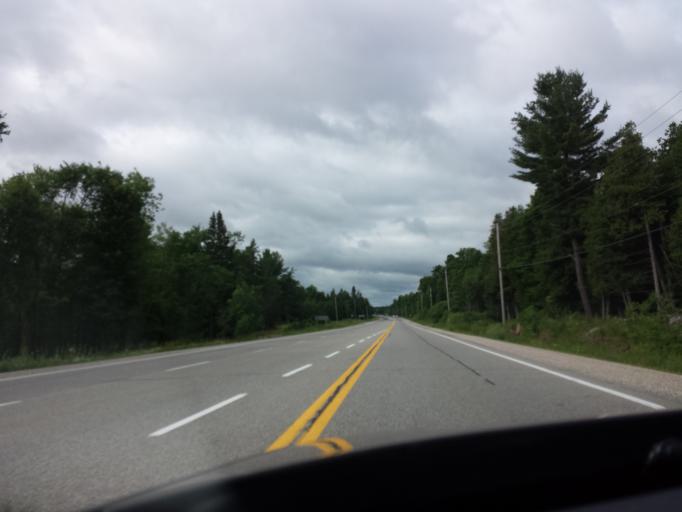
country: CA
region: Ontario
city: Carleton Place
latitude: 45.0977
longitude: -76.2378
